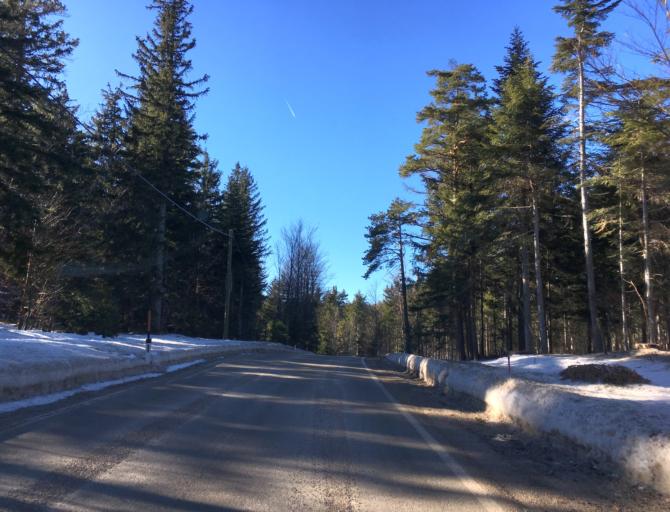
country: AT
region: Lower Austria
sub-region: Politischer Bezirk Wiener Neustadt
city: Waldegg
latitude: 47.8376
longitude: 16.0478
